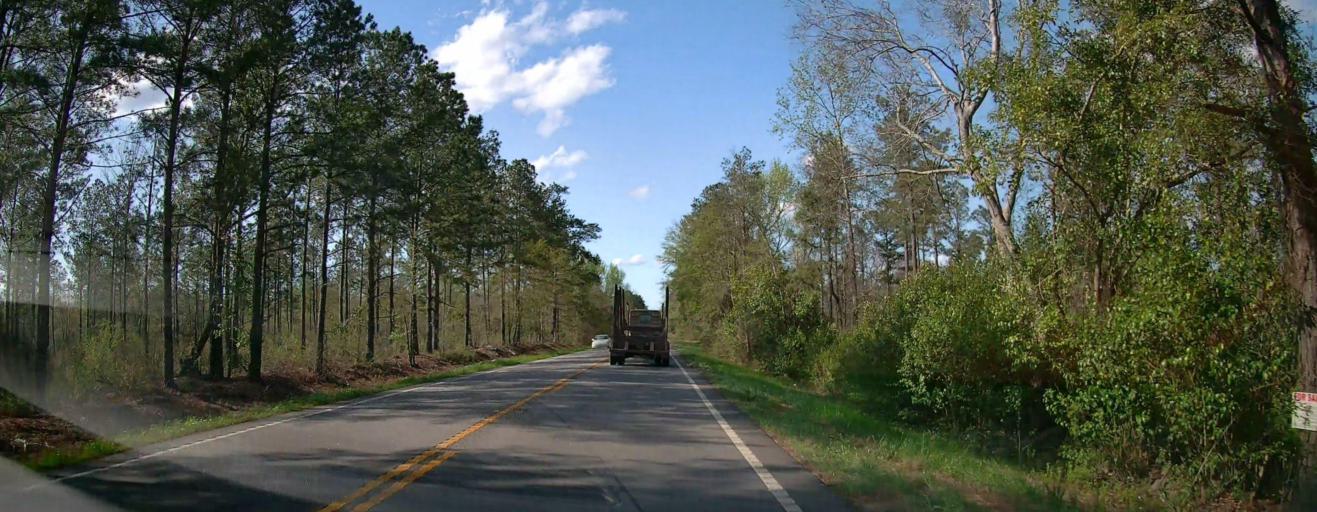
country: US
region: Georgia
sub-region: Baldwin County
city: Hardwick
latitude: 33.0482
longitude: -83.1216
